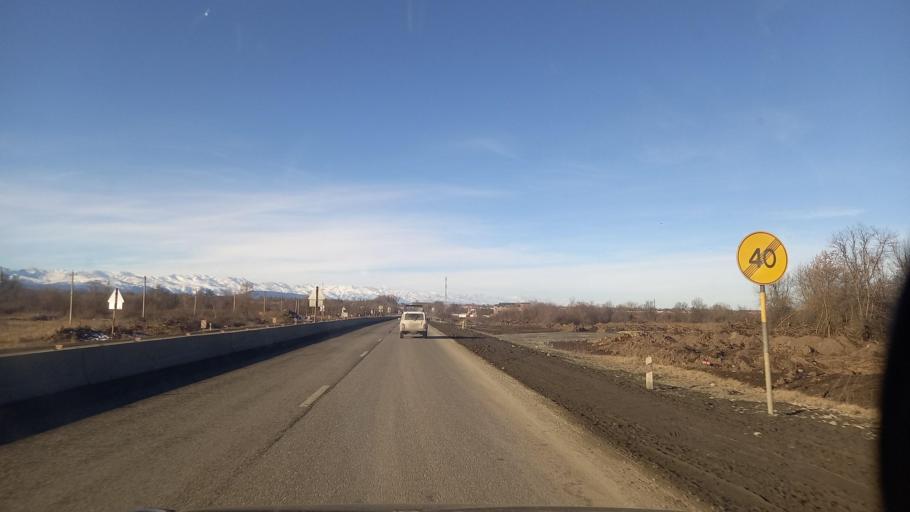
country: RU
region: North Ossetia
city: Gizel'
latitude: 43.0279
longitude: 44.6052
